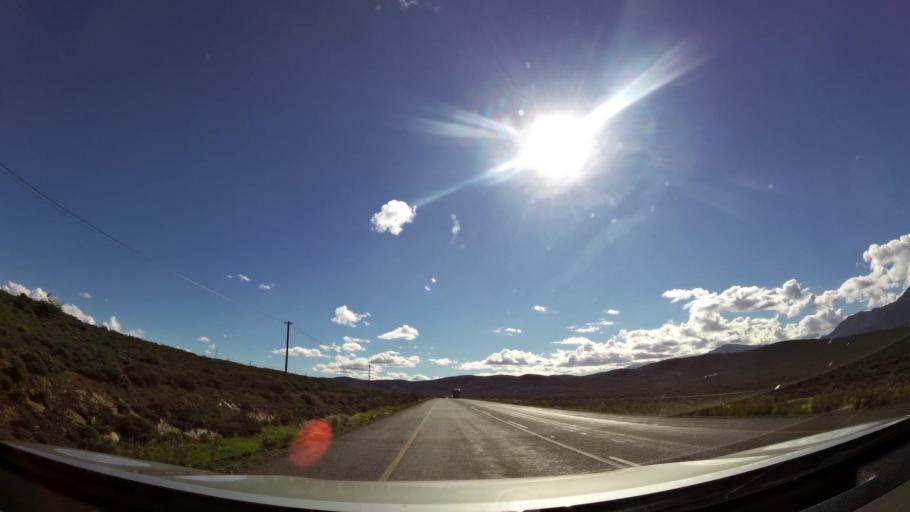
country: ZA
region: Western Cape
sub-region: Cape Winelands District Municipality
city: Worcester
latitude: -33.7438
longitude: 19.6978
